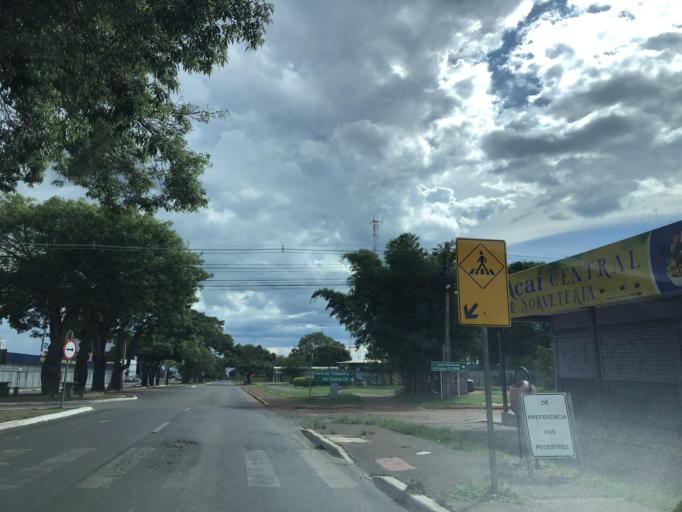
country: BR
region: Goias
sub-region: Luziania
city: Luziania
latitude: -16.0188
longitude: -48.0675
